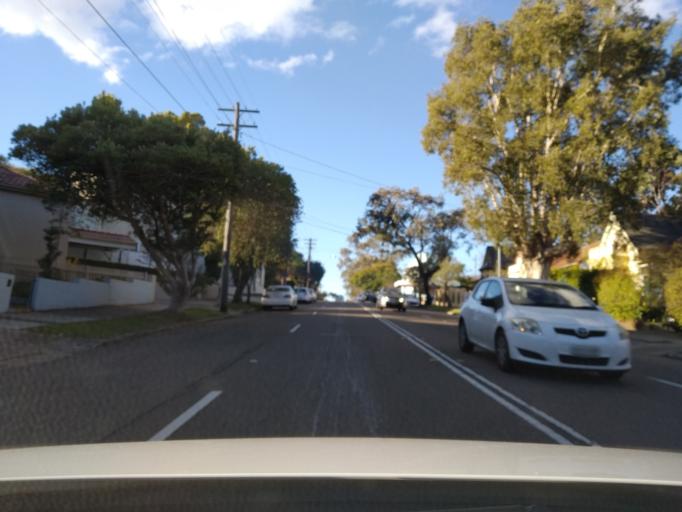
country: AU
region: New South Wales
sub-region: Ashfield
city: Summer Hill
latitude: -33.8970
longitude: 151.1366
